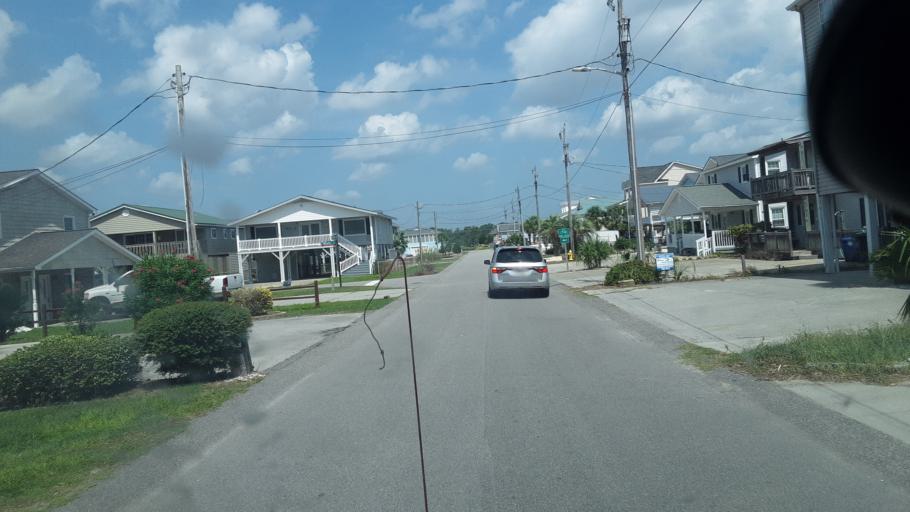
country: US
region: South Carolina
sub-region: Horry County
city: Little River
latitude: 33.8311
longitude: -78.6347
